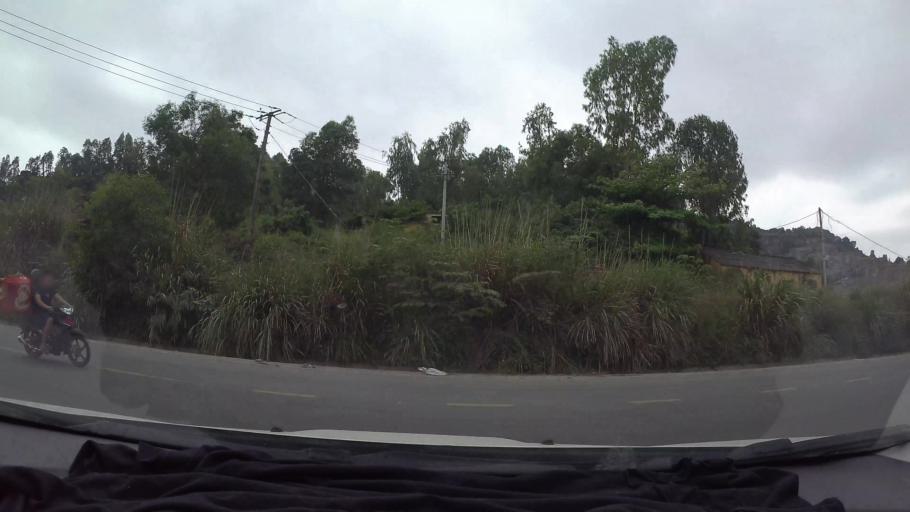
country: VN
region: Da Nang
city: Lien Chieu
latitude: 16.0396
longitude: 108.1707
